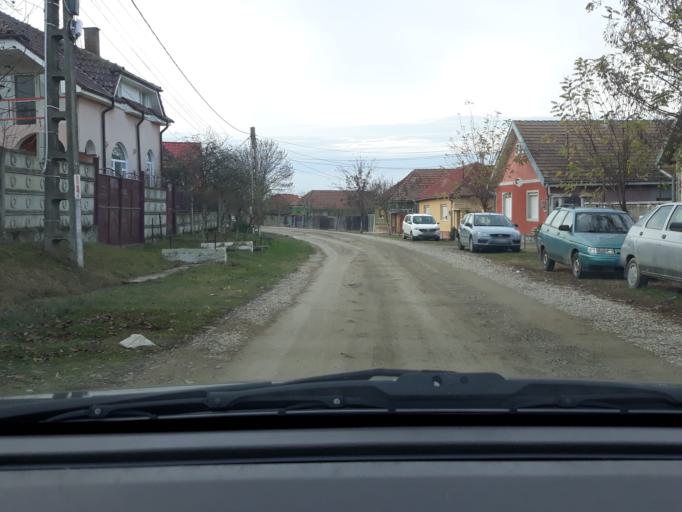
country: RO
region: Bihor
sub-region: Comuna Osorheiu
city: Alparea
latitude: 47.0137
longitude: 22.0237
